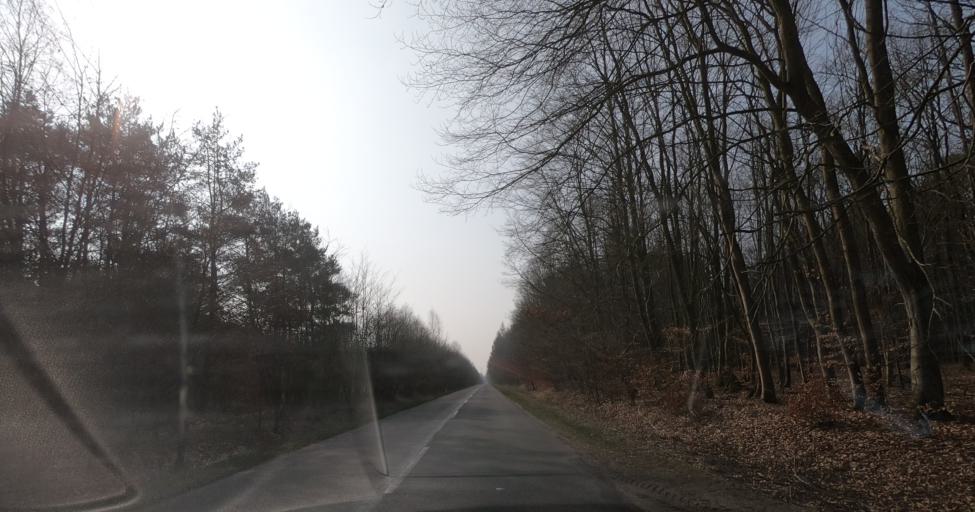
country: PL
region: West Pomeranian Voivodeship
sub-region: Powiat gryfinski
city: Banie
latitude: 53.0046
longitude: 14.7232
